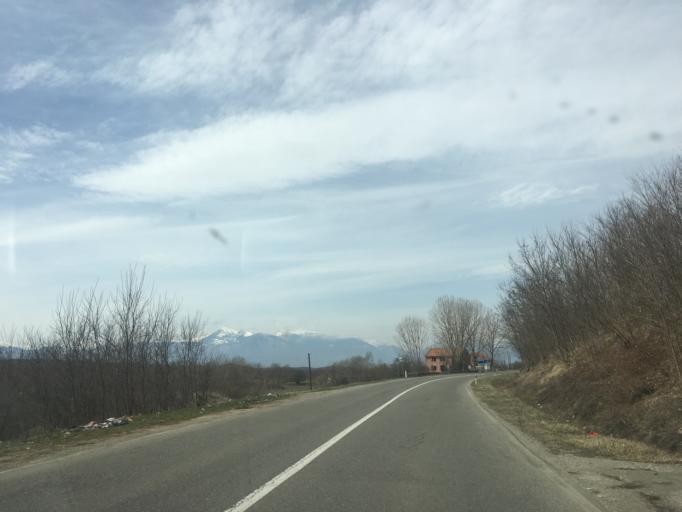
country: XK
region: Pec
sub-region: Komuna e Klines
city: Klina
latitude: 42.6004
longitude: 20.5265
